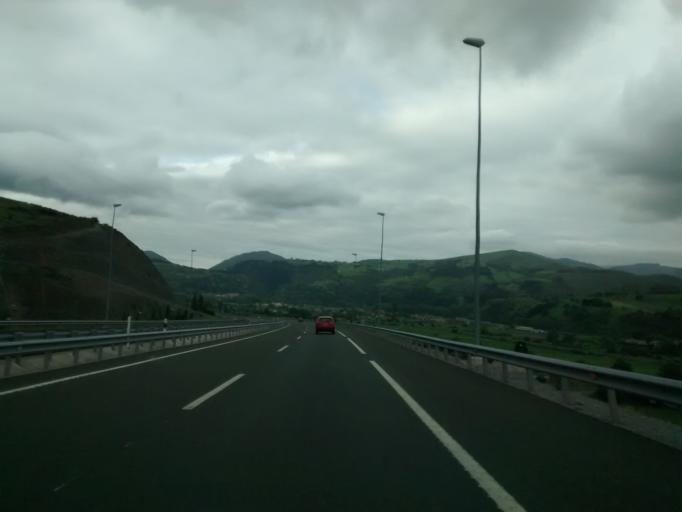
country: ES
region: Cantabria
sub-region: Provincia de Cantabria
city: Molledo
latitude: 43.1647
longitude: -4.0526
